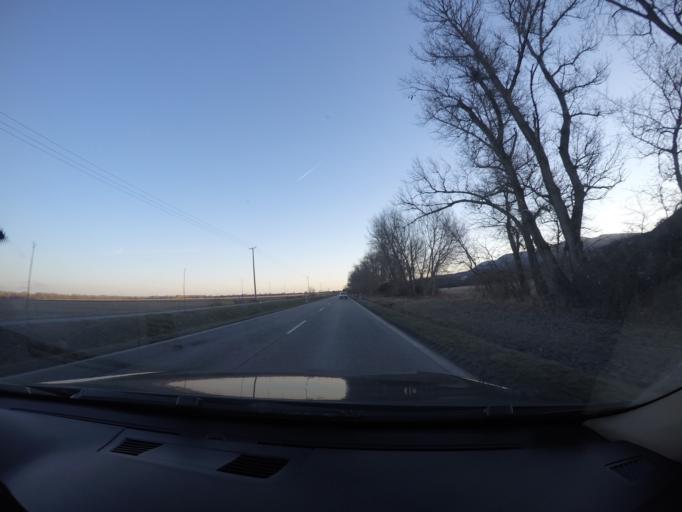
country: HU
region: Pest
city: Dunabogdany
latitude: 47.7830
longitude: 19.0479
